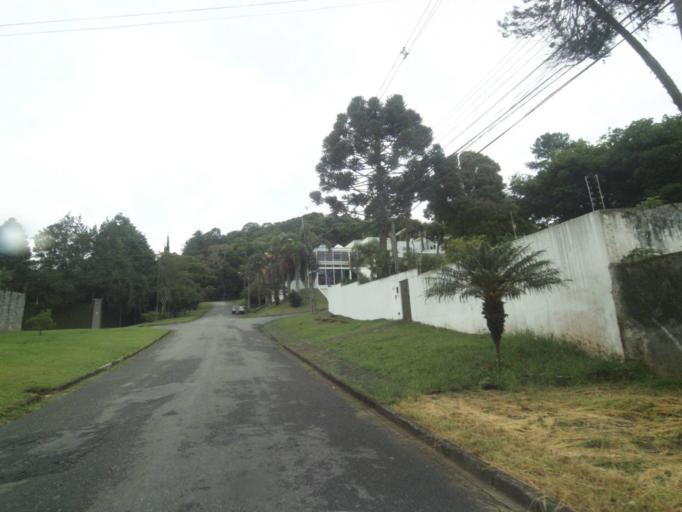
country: BR
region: Parana
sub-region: Curitiba
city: Curitiba
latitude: -25.4282
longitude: -49.3169
